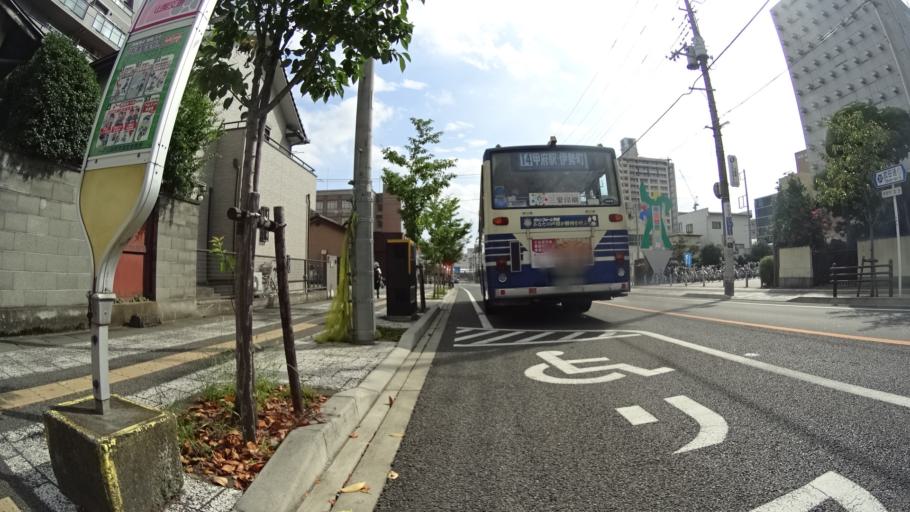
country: JP
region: Yamanashi
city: Kofu-shi
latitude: 35.6711
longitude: 138.5703
